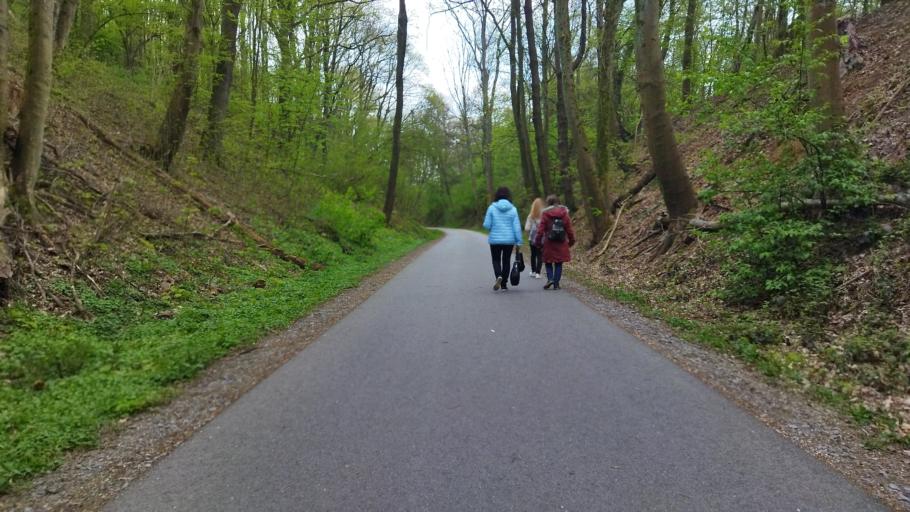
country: DE
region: North Rhine-Westphalia
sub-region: Regierungsbezirk Dusseldorf
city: Heiligenhaus
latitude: 51.3318
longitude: 6.9466
